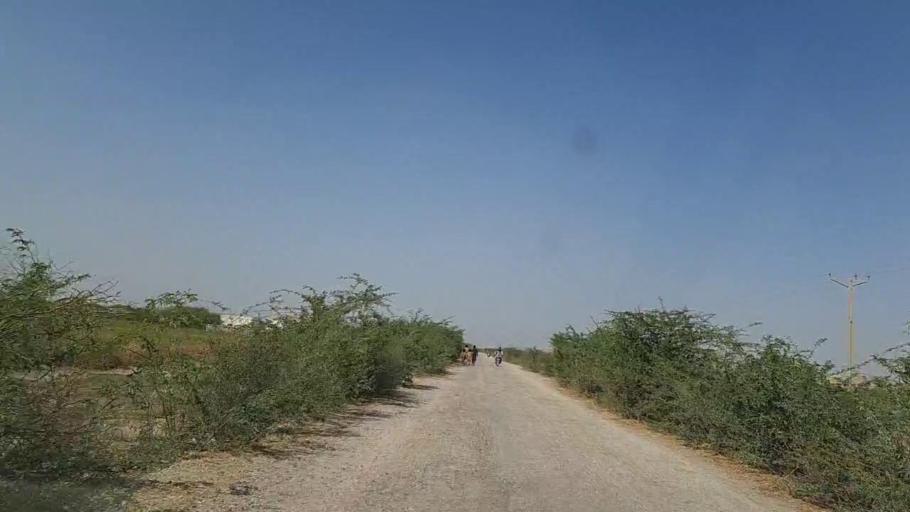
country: PK
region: Sindh
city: Naukot
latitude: 24.6258
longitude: 69.2889
